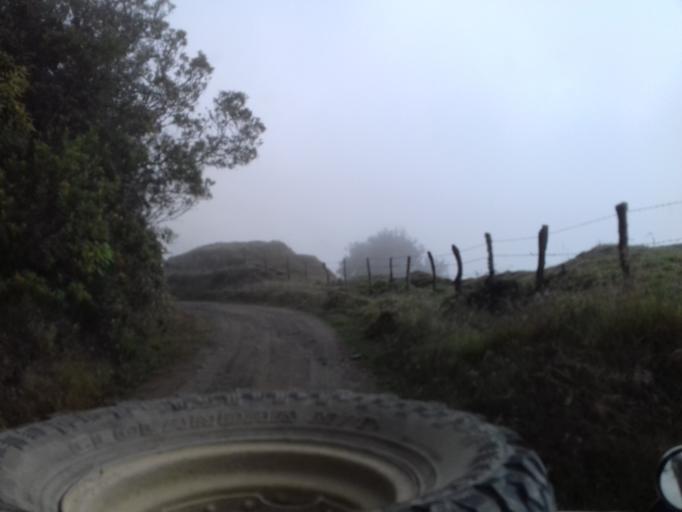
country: CO
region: Quindio
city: Salento
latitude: 4.5523
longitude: -75.5070
